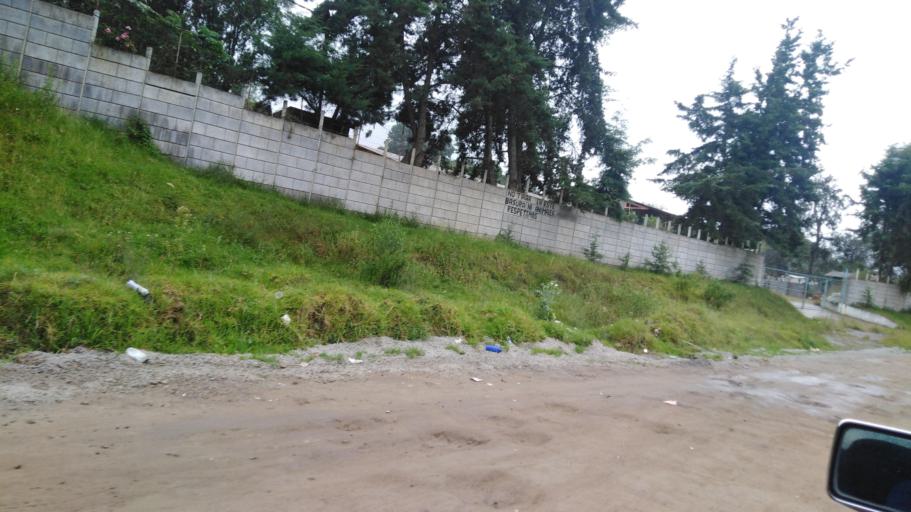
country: GT
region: Quetzaltenango
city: Quetzaltenango
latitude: 14.8556
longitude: -91.5046
